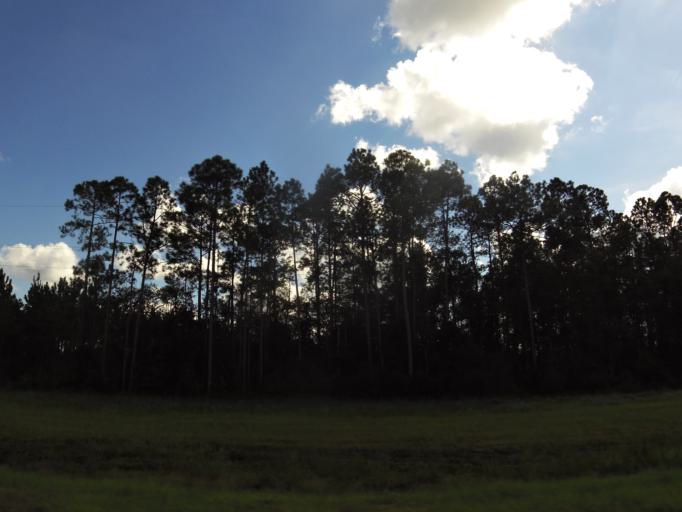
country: US
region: Florida
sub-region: Hamilton County
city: Jasper
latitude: 30.6757
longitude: -82.6346
